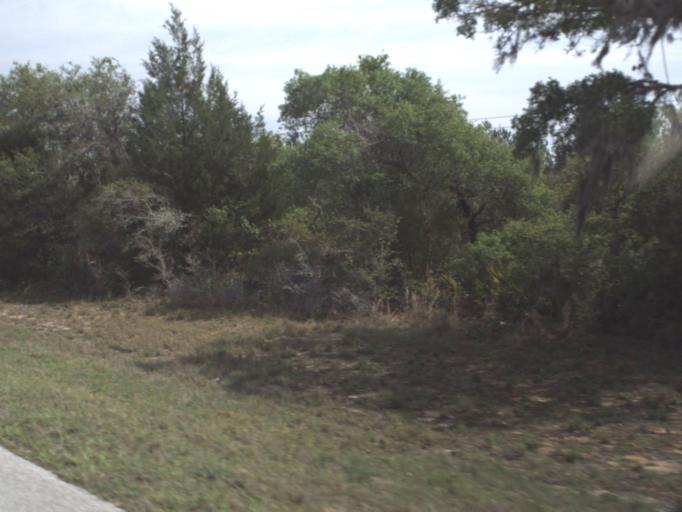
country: US
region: Florida
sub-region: Lake County
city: Astor
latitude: 29.2361
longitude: -81.6462
